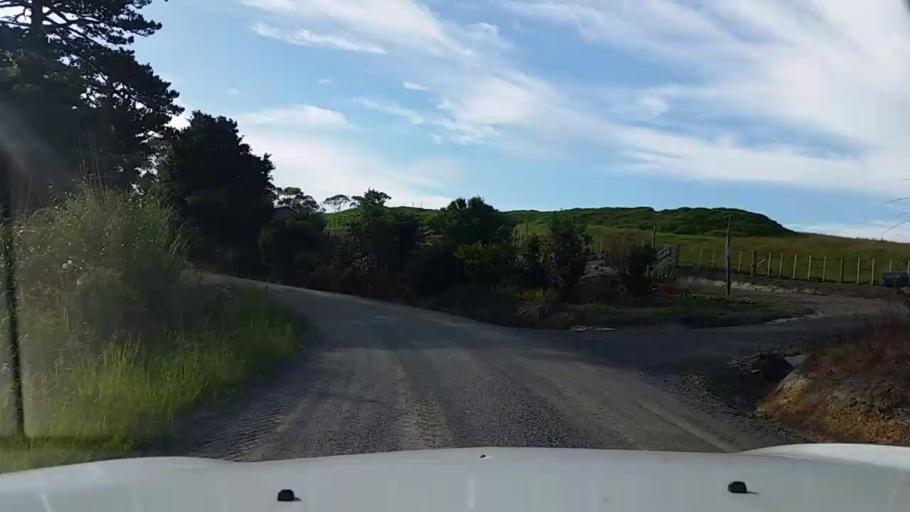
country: NZ
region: Northland
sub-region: Whangarei
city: Maungatapere
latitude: -35.6686
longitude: 174.1746
